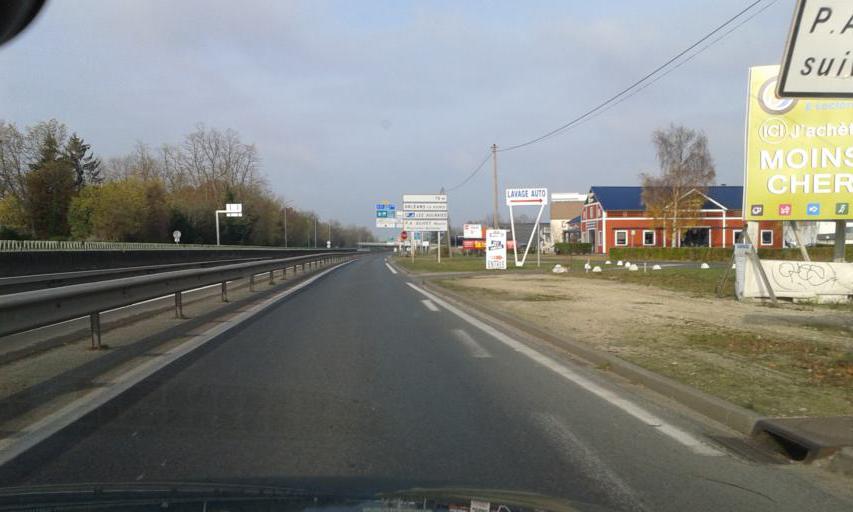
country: FR
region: Centre
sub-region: Departement du Loiret
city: Olivet
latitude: 47.8408
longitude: 1.9139
